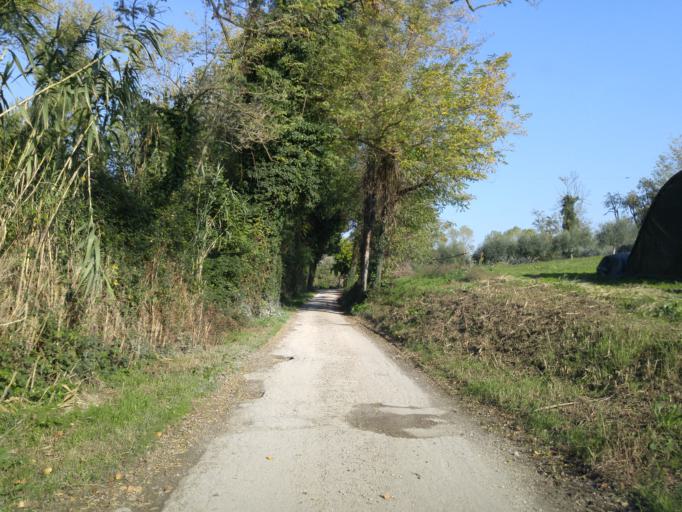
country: IT
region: The Marches
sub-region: Provincia di Pesaro e Urbino
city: Calcinelli
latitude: 43.7447
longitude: 12.9247
